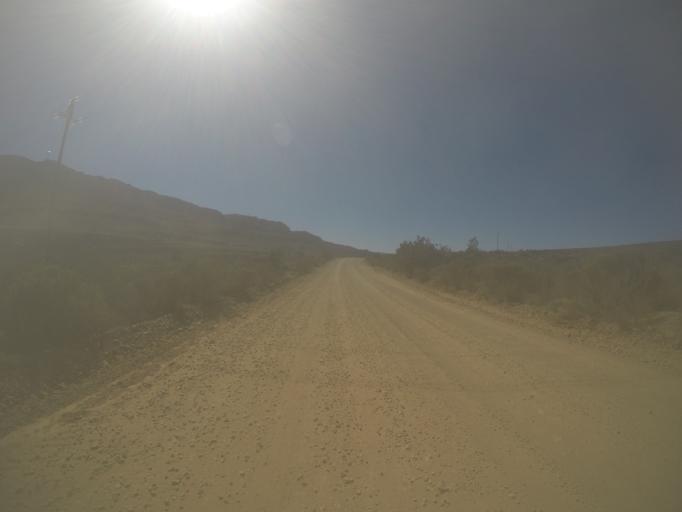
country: ZA
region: Western Cape
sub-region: West Coast District Municipality
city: Clanwilliam
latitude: -32.4954
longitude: 19.2680
